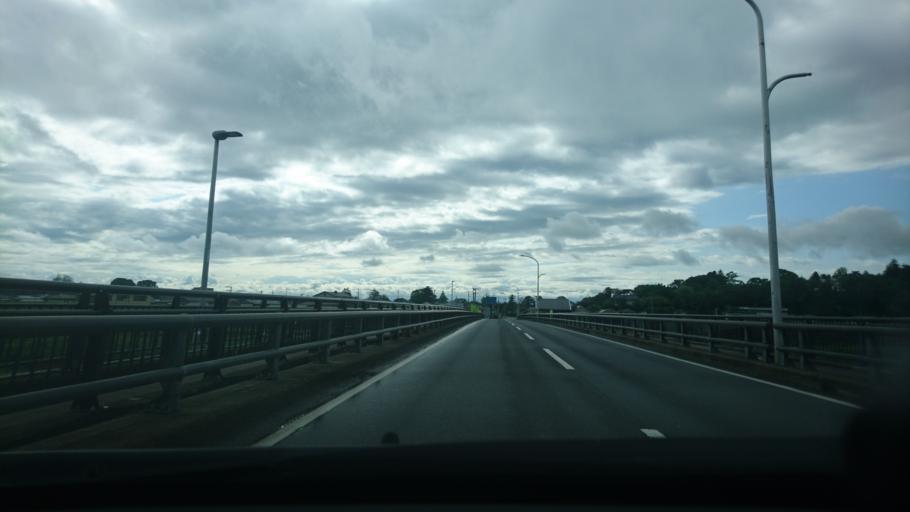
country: JP
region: Miyagi
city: Wakuya
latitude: 38.6531
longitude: 141.2858
